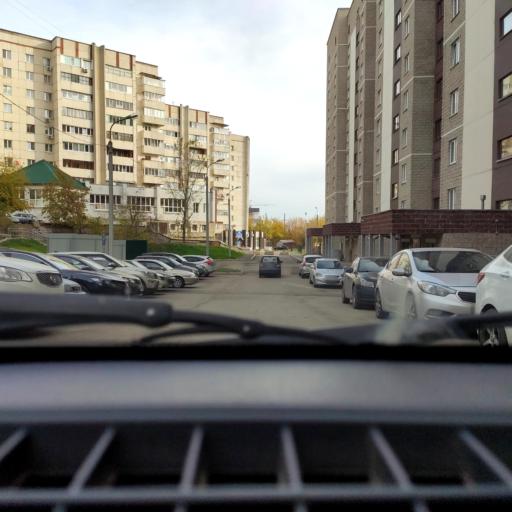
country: RU
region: Bashkortostan
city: Ufa
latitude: 54.7766
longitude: 56.0413
